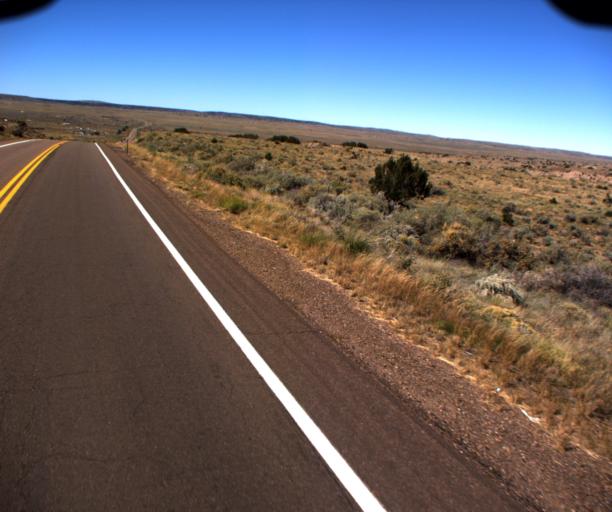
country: US
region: Arizona
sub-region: Apache County
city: Saint Johns
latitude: 34.5060
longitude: -109.4127
